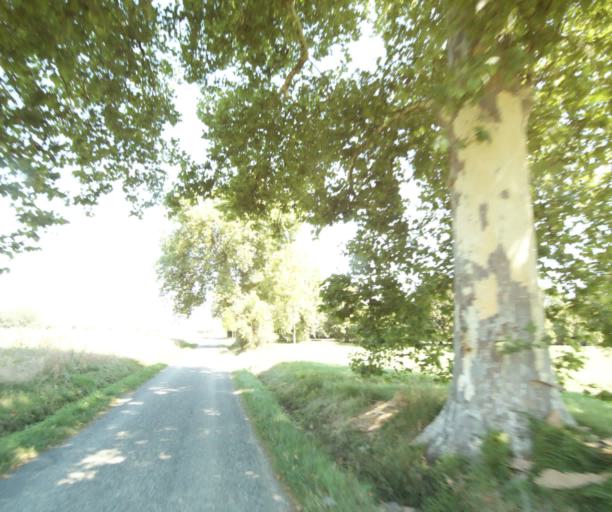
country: FR
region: Midi-Pyrenees
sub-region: Departement de l'Ariege
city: Lezat-sur-Leze
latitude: 43.2757
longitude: 1.3565
